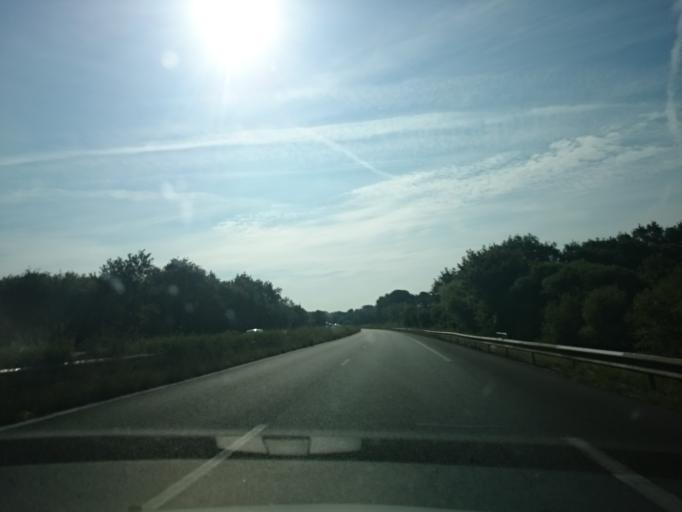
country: FR
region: Brittany
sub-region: Departement du Finistere
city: Le Trevoux
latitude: 47.8779
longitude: -3.6624
